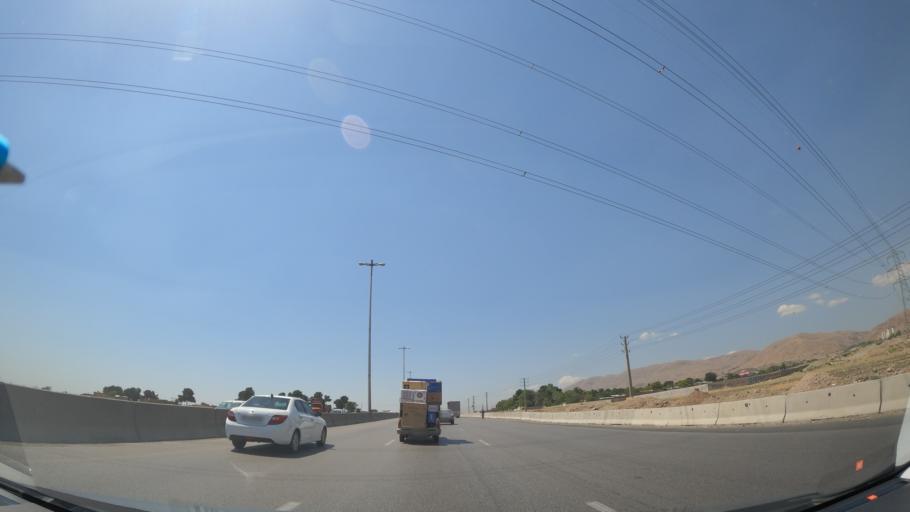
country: IR
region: Alborz
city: Karaj
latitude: 35.8712
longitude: 50.8971
